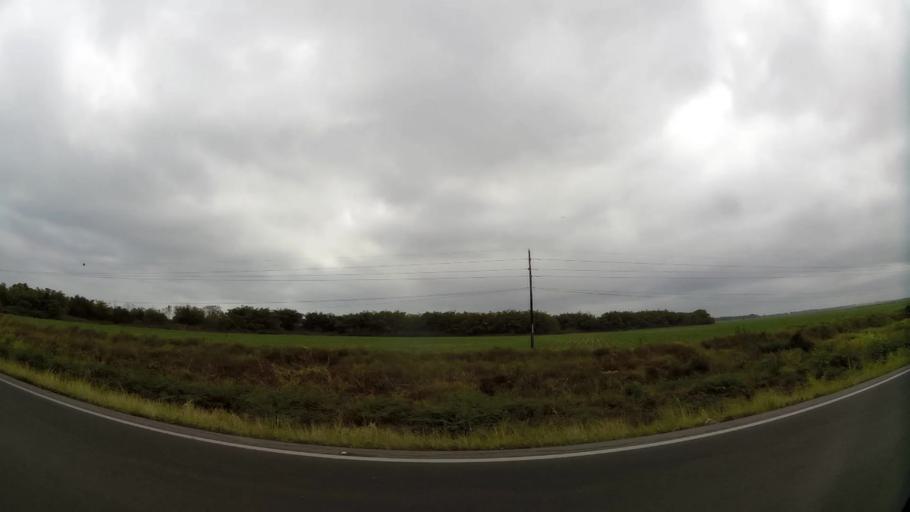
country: EC
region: Guayas
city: Yaguachi Nuevo
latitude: -2.3023
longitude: -79.6385
